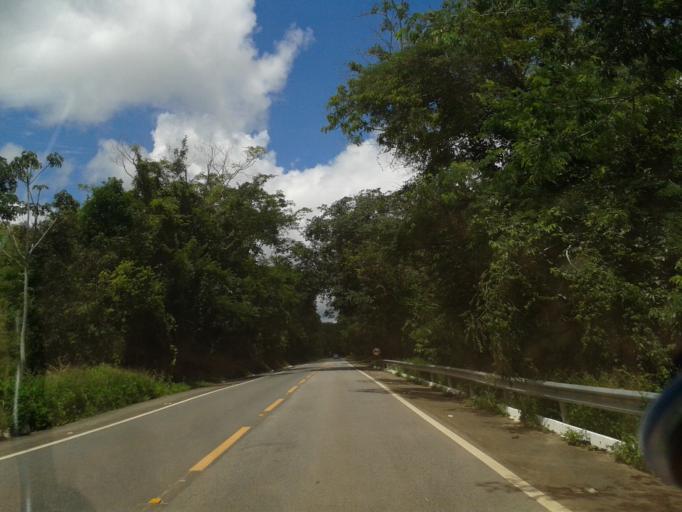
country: BR
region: Goias
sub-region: Goias
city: Goias
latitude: -15.8978
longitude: -50.1087
